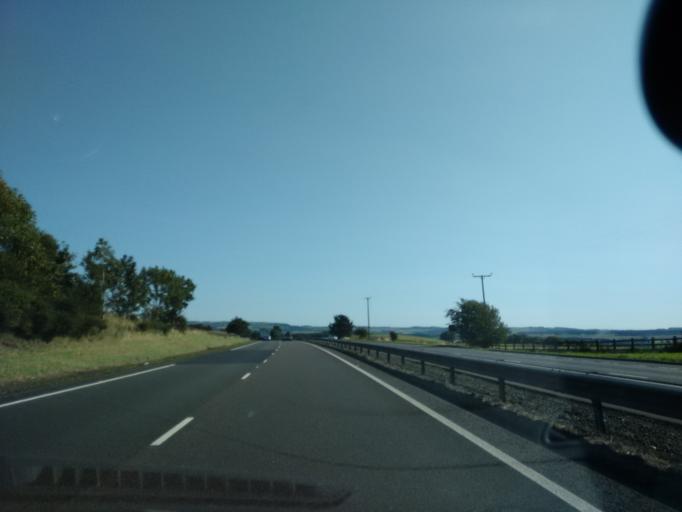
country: GB
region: England
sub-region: Northumberland
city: Corbridge
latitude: 54.9723
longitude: -1.9812
